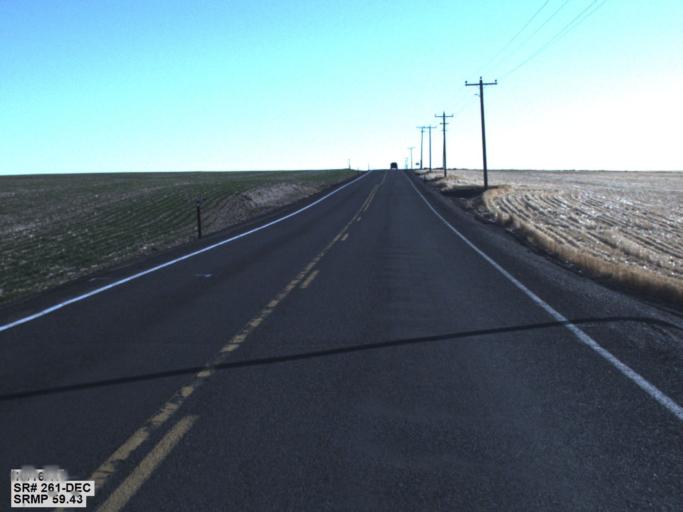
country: US
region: Washington
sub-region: Adams County
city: Ritzville
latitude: 47.0679
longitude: -118.3653
